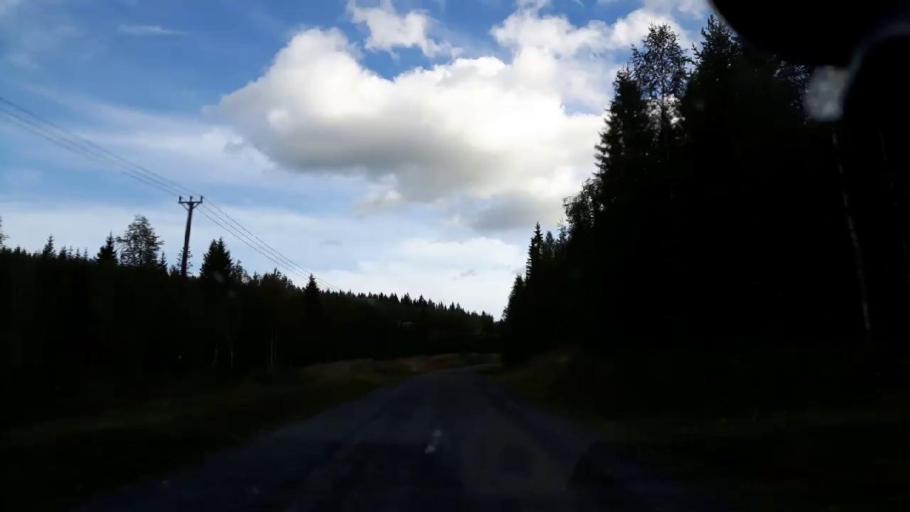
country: SE
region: Jaemtland
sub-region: Ragunda Kommun
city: Hammarstrand
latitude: 63.4189
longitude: 16.0737
